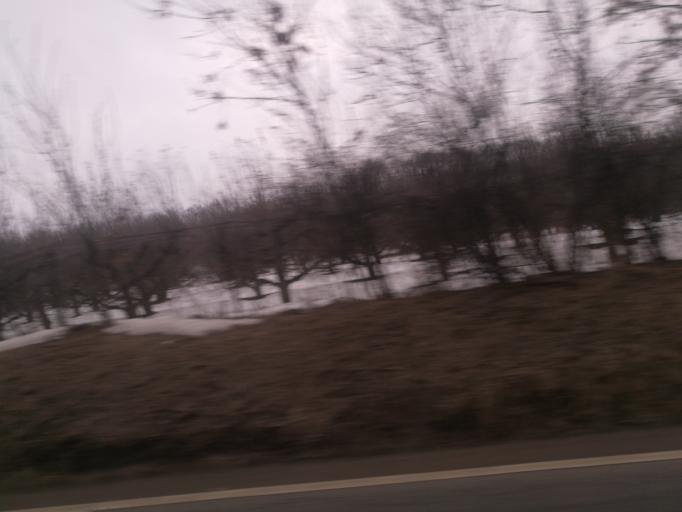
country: RO
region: Suceava
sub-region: Municipiul Falticeni
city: Falticeni
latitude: 47.4377
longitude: 26.2976
